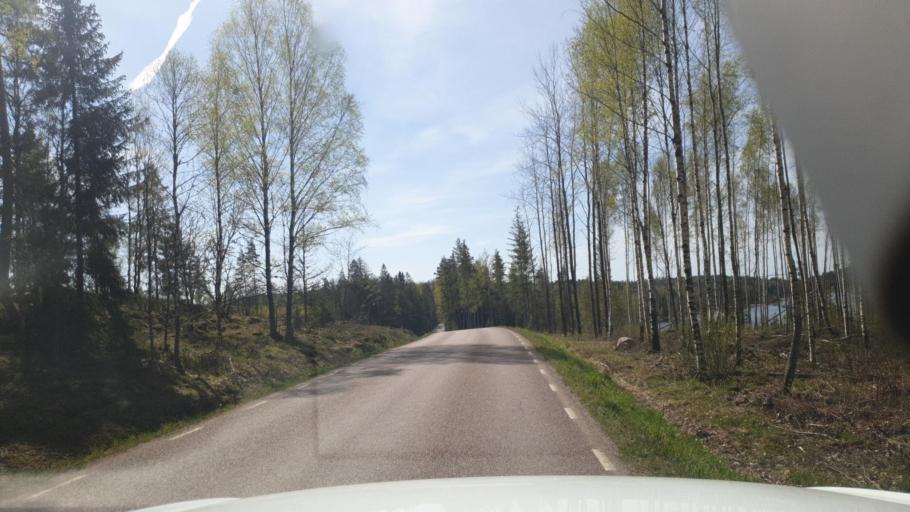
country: SE
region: Vaermland
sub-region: Grums Kommun
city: Grums
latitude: 59.4242
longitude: 13.0867
